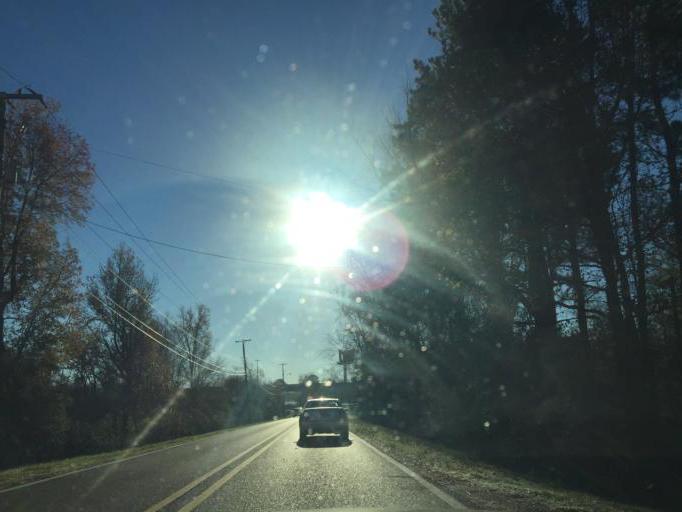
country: US
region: Mississippi
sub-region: Hinds County
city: Jackson
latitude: 32.2849
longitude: -90.1737
